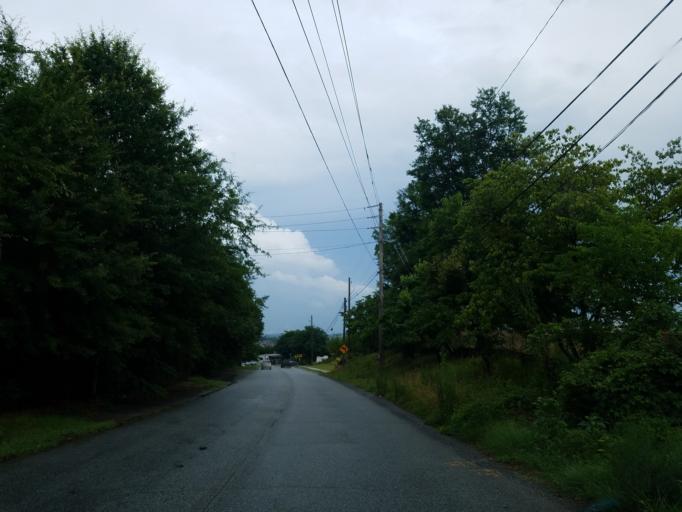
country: US
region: Georgia
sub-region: Cobb County
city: Vinings
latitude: 33.8467
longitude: -84.4933
